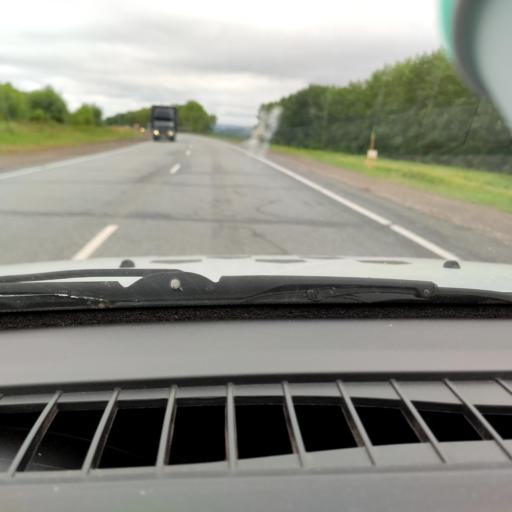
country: RU
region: Tatarstan
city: Mendeleyevsk
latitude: 55.8430
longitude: 52.2027
